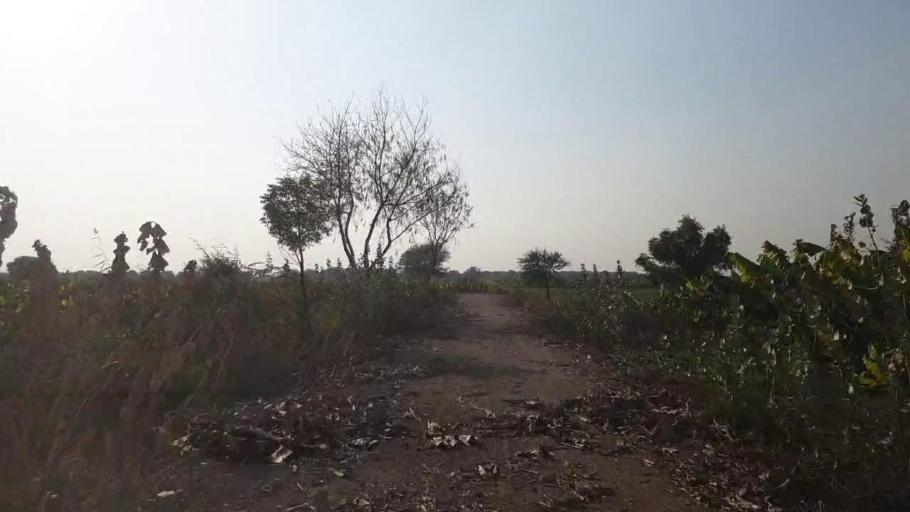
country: PK
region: Sindh
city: Mirpur Khas
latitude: 25.4172
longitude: 68.9451
